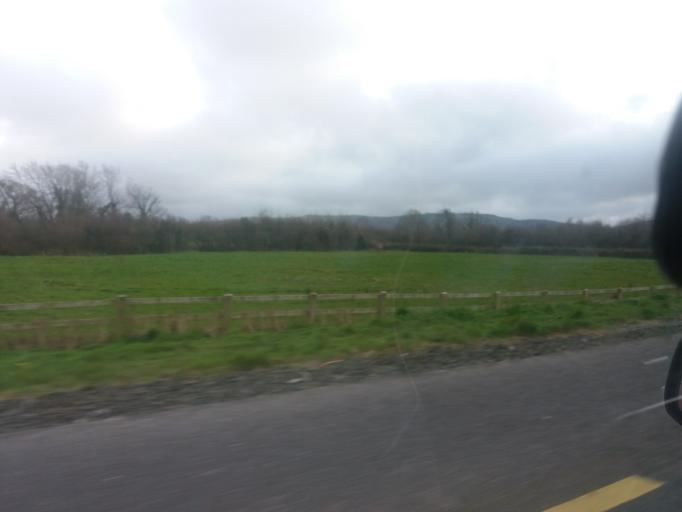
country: IE
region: Munster
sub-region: County Limerick
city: Newcastle West
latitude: 52.4359
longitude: -9.1012
